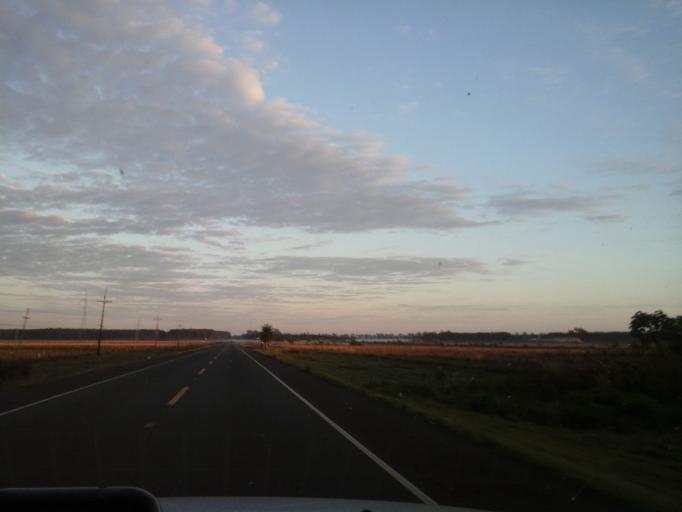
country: PY
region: Itapua
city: General Delgado
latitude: -27.0685
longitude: -56.6120
